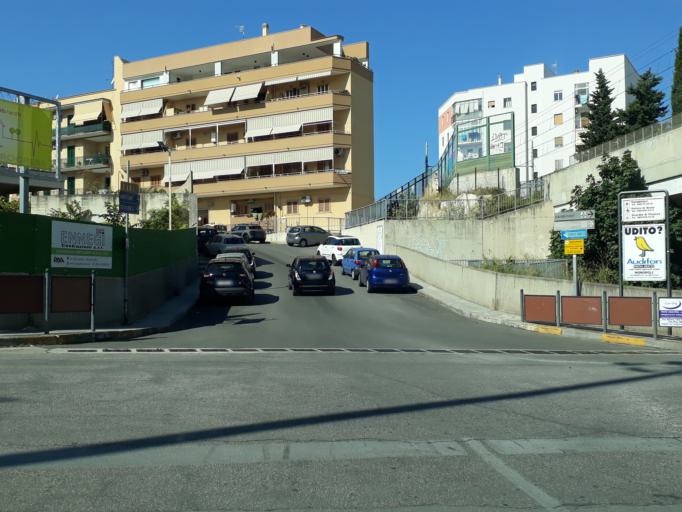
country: IT
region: Apulia
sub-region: Provincia di Bari
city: Monopoli
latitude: 40.9501
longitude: 17.2963
